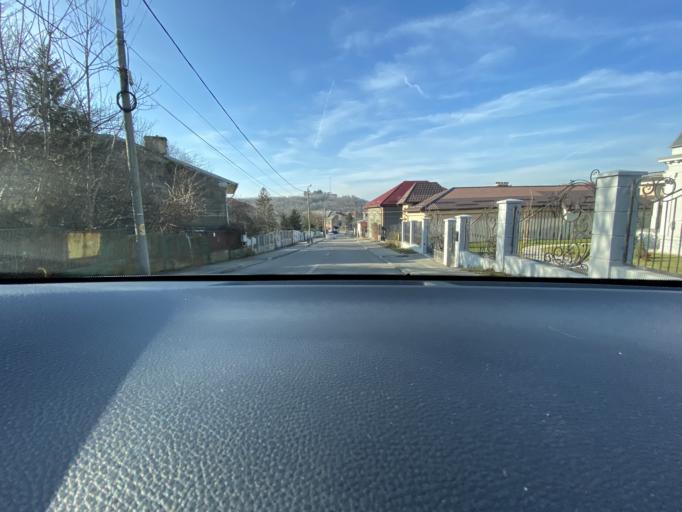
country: RO
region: Olt
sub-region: Municipiul Slatina
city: Slatina
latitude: 44.4281
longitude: 24.3587
